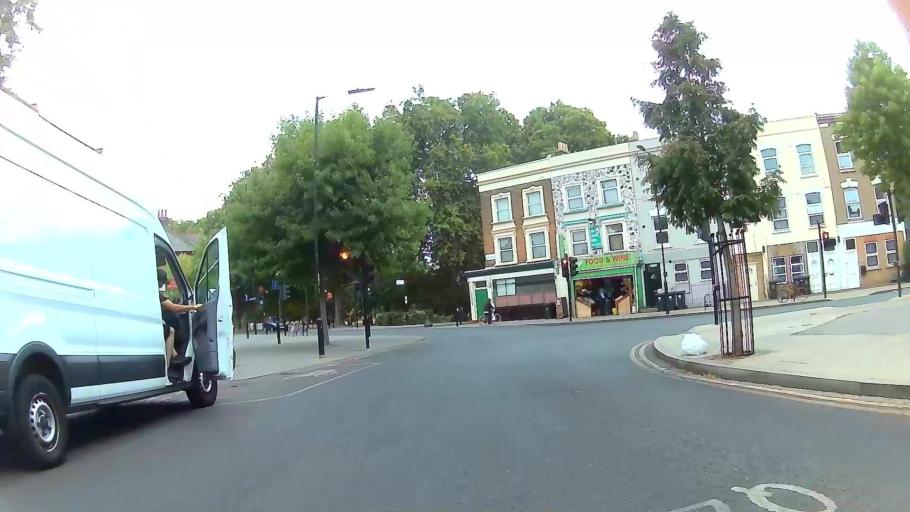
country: GB
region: England
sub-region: Greater London
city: Hackney
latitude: 51.5567
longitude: -0.0467
